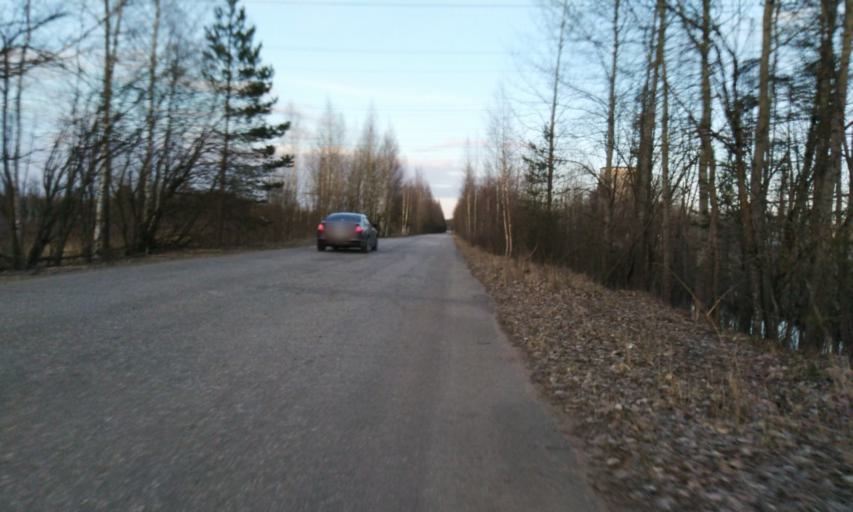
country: RU
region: Leningrad
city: Novoye Devyatkino
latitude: 60.0789
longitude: 30.4786
